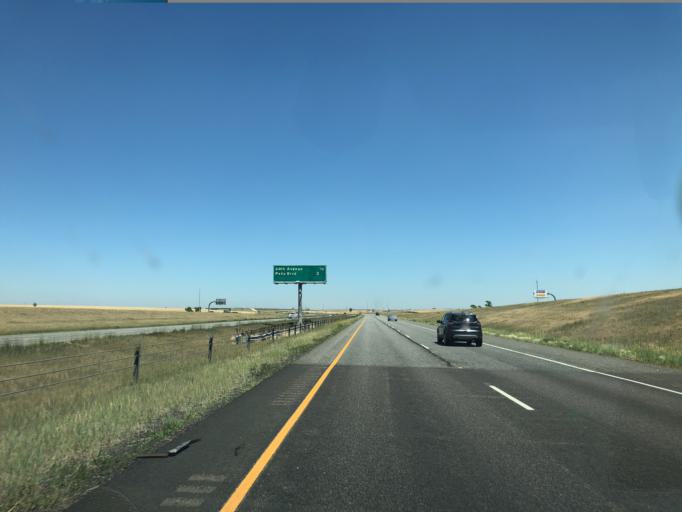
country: US
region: Colorado
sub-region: Adams County
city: Aurora
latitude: 39.7990
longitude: -104.7161
